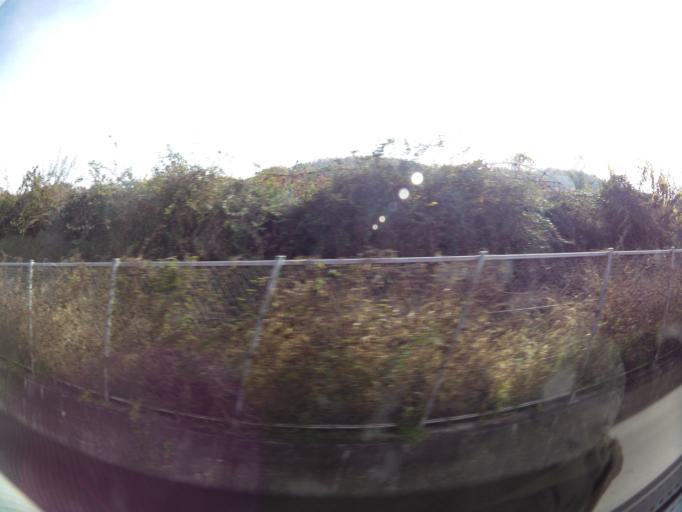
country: KR
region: Daejeon
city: Daejeon
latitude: 36.3327
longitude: 127.4799
